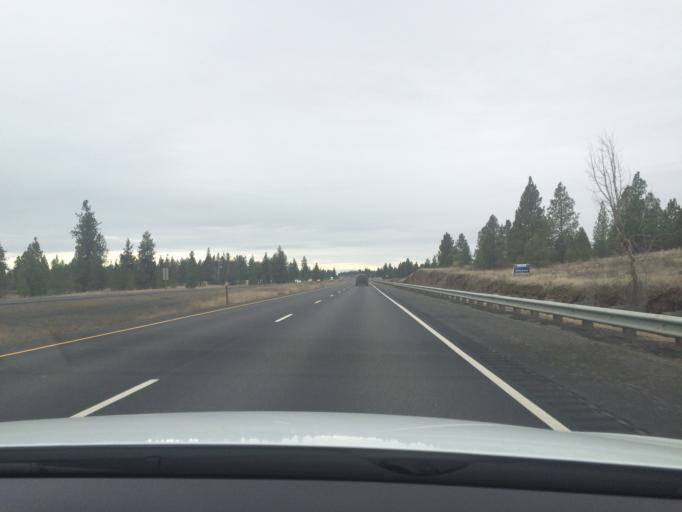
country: US
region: Washington
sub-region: Spokane County
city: Medical Lake
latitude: 47.4467
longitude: -117.7763
